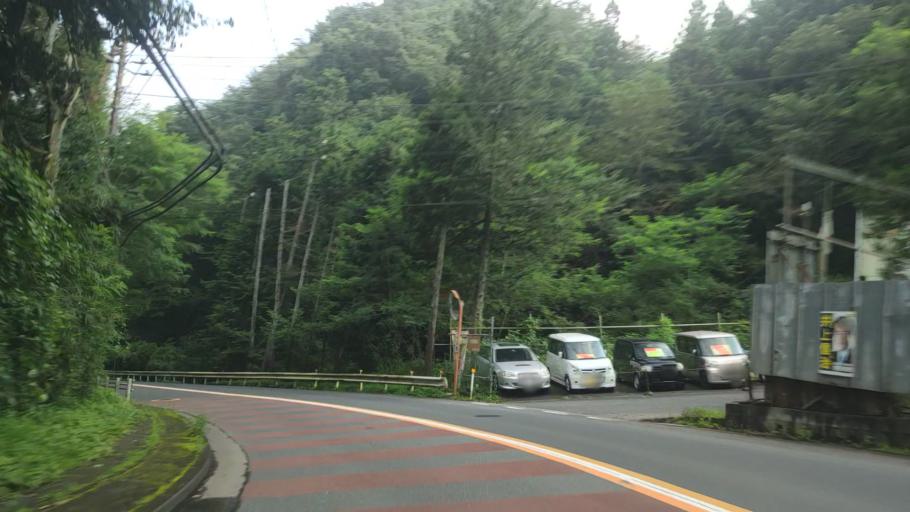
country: JP
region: Saitama
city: Hanno
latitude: 35.8243
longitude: 139.2748
